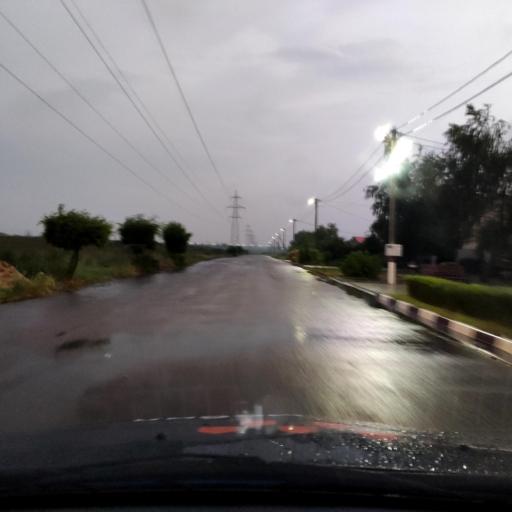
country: RU
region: Voronezj
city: Novaya Usman'
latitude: 51.6233
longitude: 39.3311
